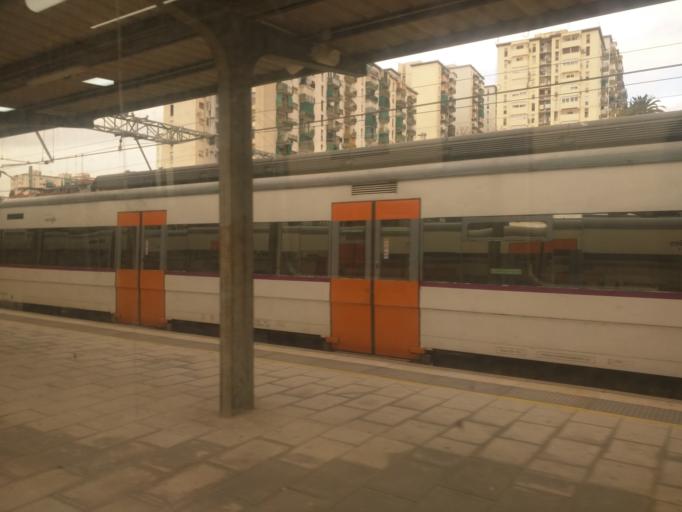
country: ES
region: Catalonia
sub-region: Provincia de Barcelona
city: L'Hospitalet de Llobregat
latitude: 41.3645
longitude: 2.1021
